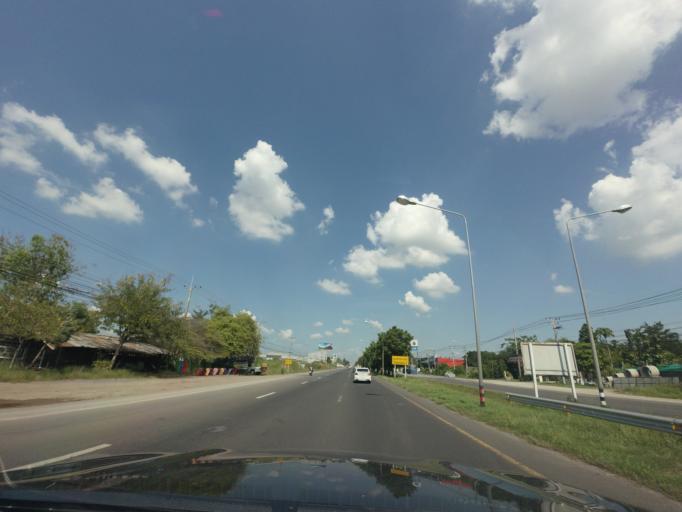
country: TH
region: Nakhon Ratchasima
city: Nakhon Ratchasima
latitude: 15.0592
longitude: 102.1691
